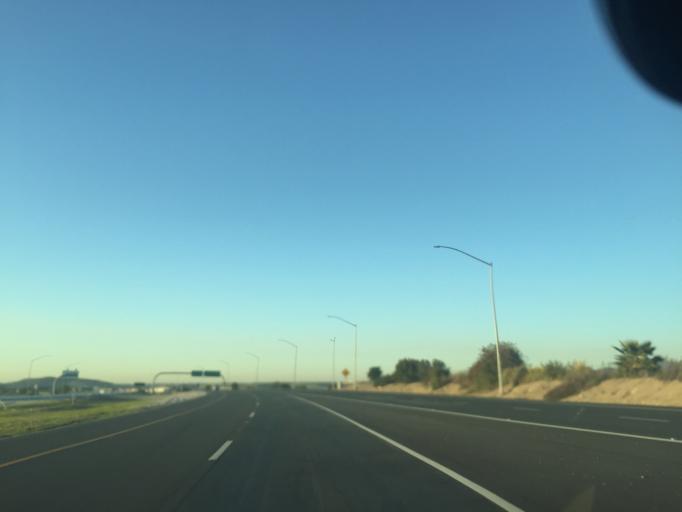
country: MX
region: Baja California
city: Tijuana
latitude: 32.5709
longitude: -116.9498
